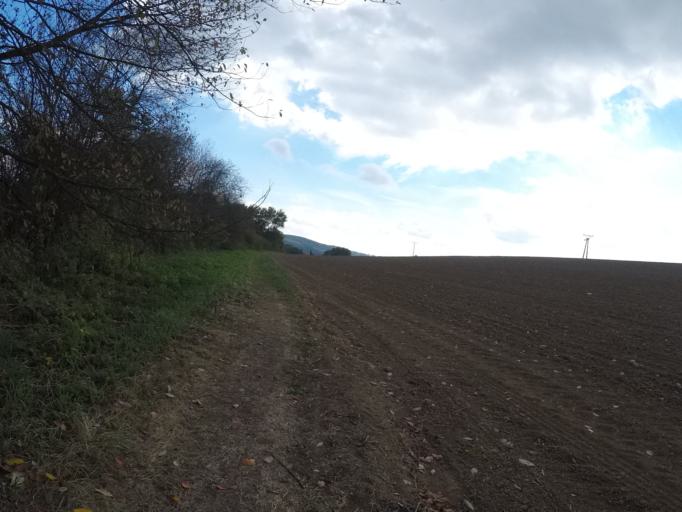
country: SK
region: Presovsky
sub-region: Okres Presov
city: Presov
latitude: 48.9303
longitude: 21.1825
